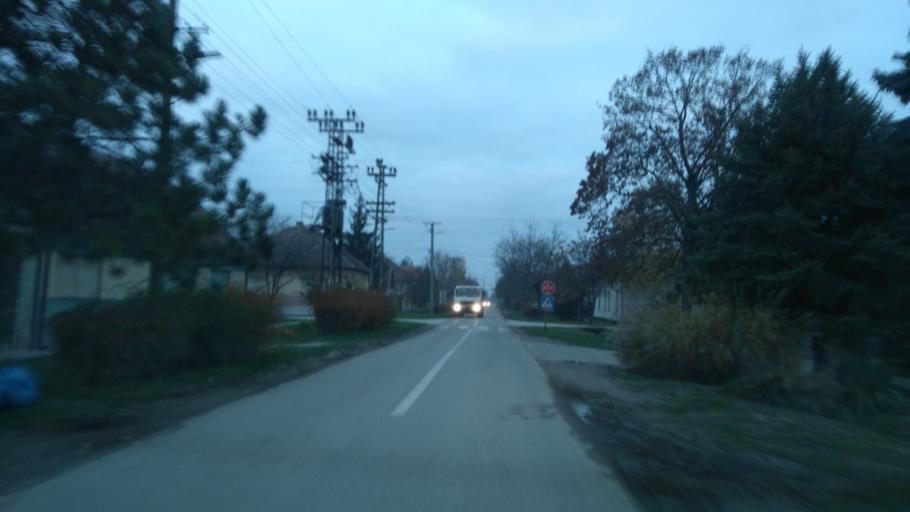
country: RS
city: Mol
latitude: 45.7650
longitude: 20.1362
